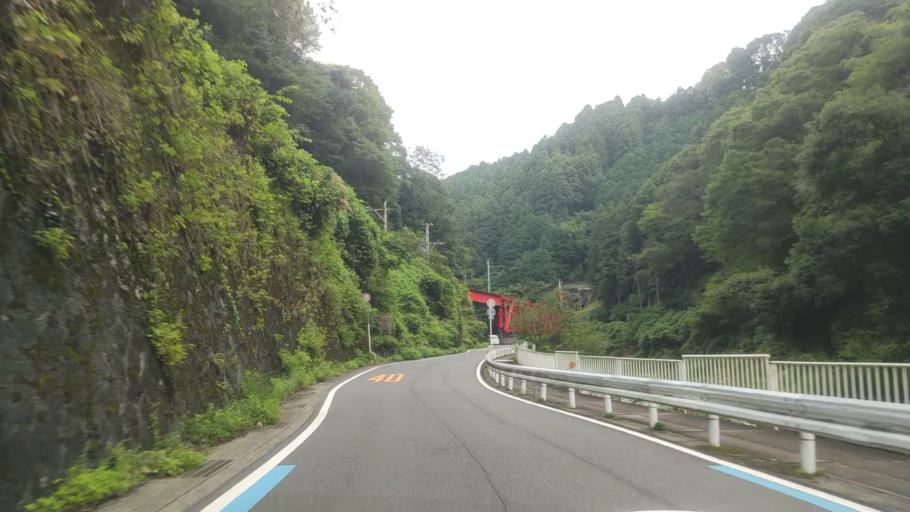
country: JP
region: Wakayama
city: Hashimoto
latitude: 34.2780
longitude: 135.5642
